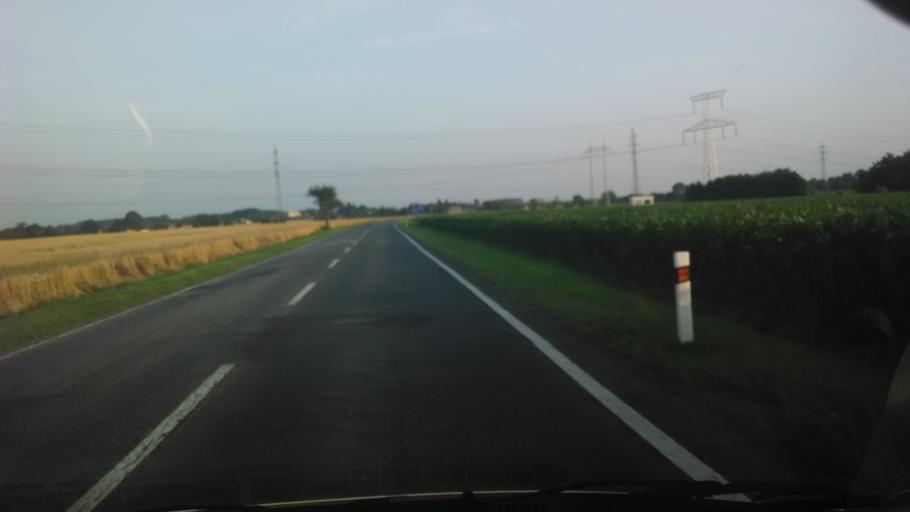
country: SK
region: Nitriansky
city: Tlmace
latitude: 48.2195
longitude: 18.5195
